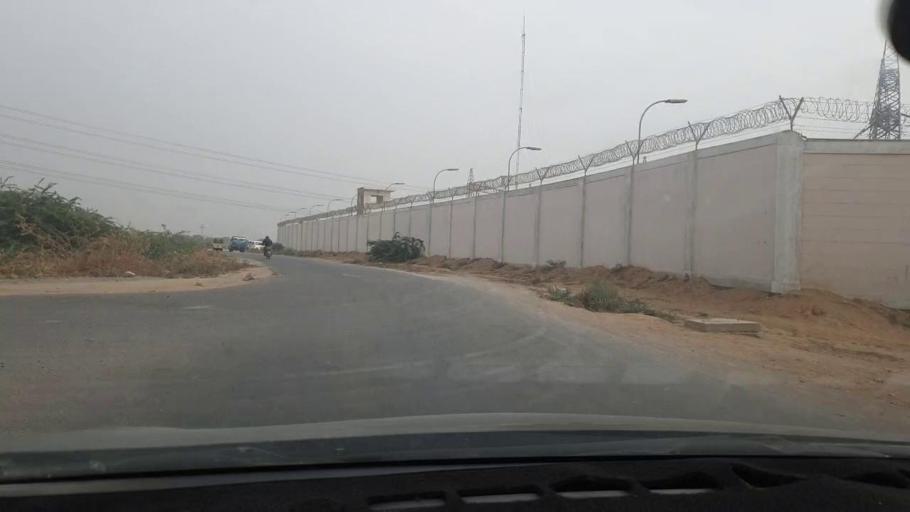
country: PK
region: Sindh
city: Malir Cantonment
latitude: 24.9117
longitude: 67.2814
